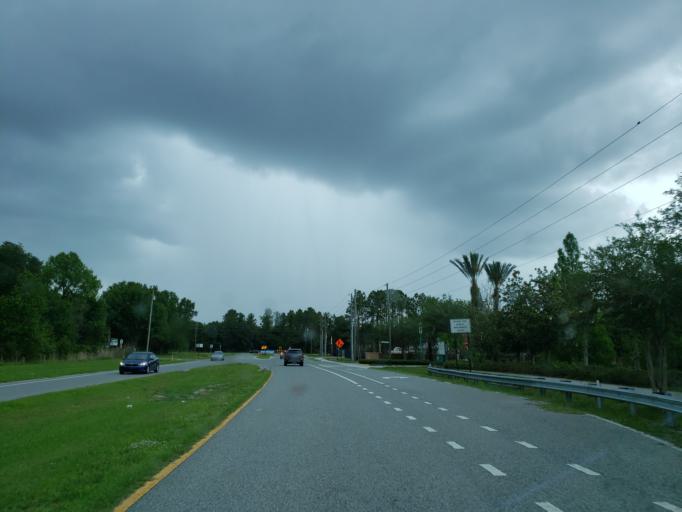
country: US
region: Florida
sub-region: Pasco County
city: Wesley Chapel
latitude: 28.2468
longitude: -82.3526
